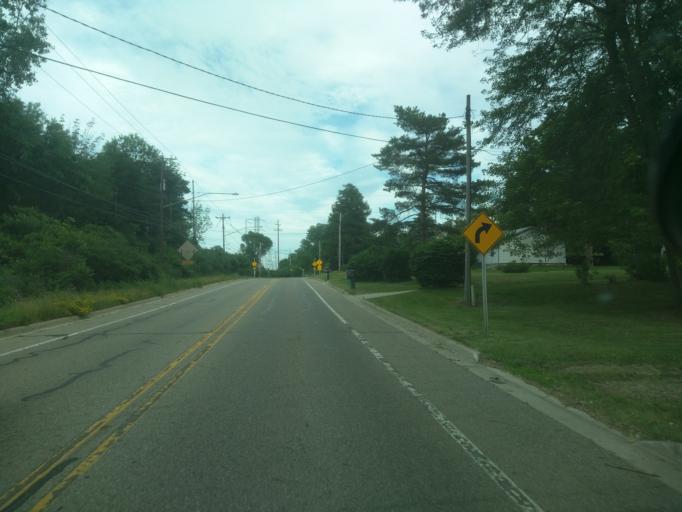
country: US
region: Michigan
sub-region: Ingham County
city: Holt
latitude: 42.6901
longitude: -84.5205
